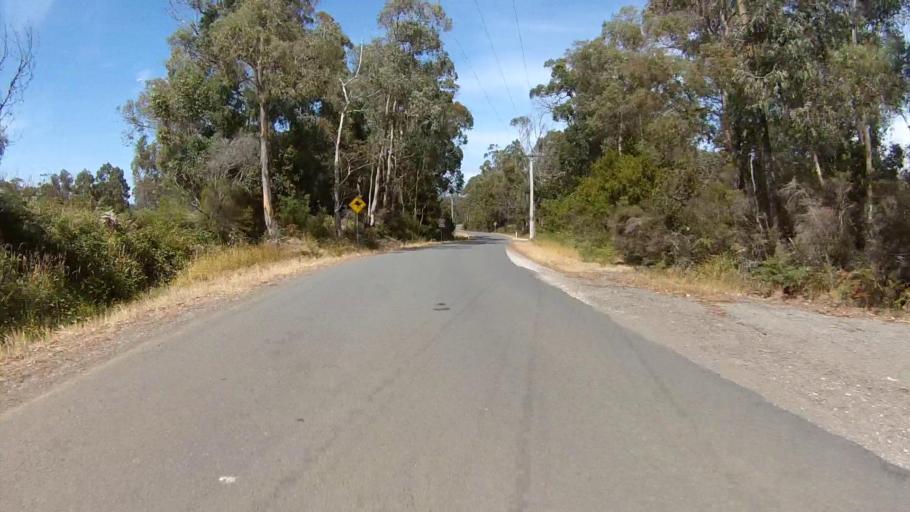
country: AU
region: Tasmania
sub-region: Huon Valley
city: Cygnet
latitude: -43.2390
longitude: 147.1246
